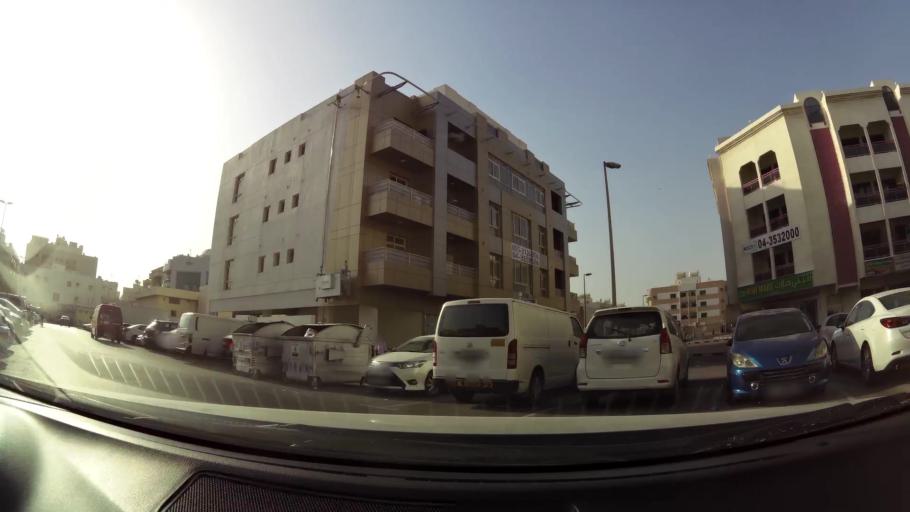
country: AE
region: Ash Shariqah
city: Sharjah
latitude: 25.2466
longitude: 55.3046
